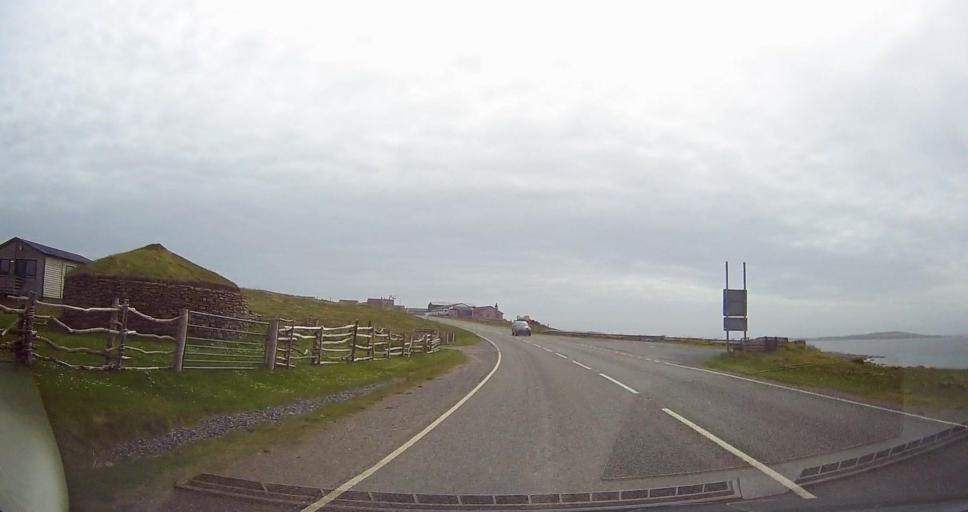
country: GB
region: Scotland
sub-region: Shetland Islands
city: Sandwick
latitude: 59.8794
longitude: -1.3061
